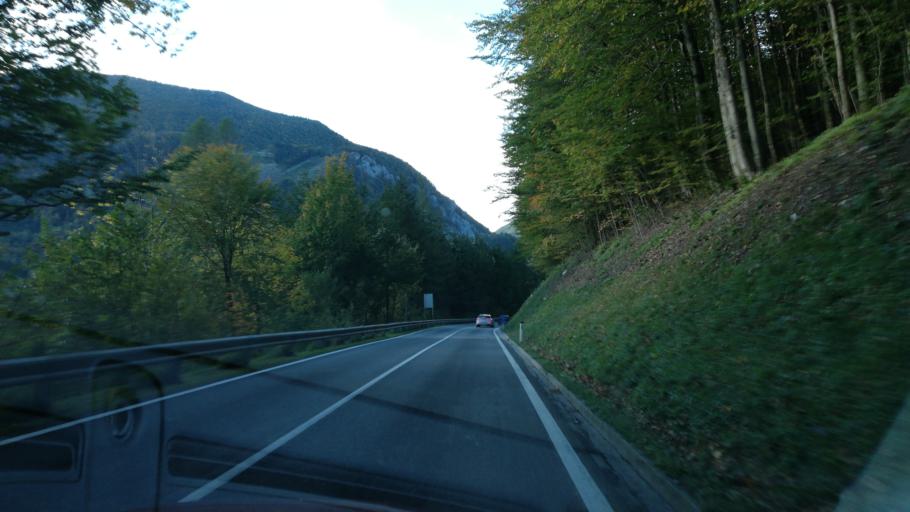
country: AT
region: Upper Austria
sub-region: Politischer Bezirk Steyr-Land
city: Weyer
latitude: 47.8551
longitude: 14.6194
